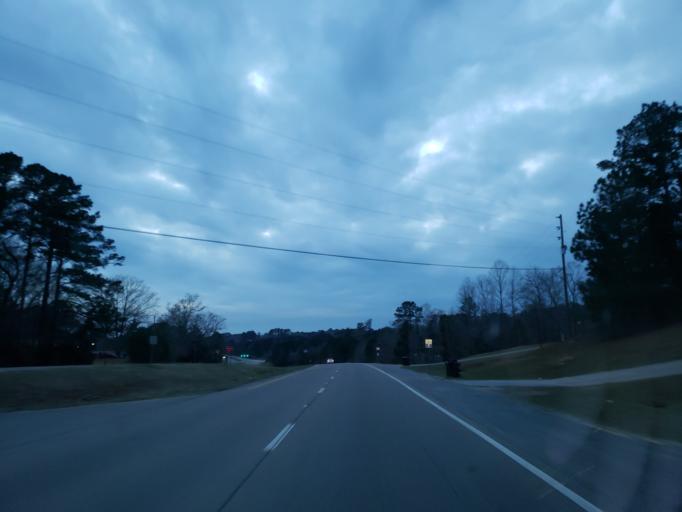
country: US
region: Mississippi
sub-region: Lauderdale County
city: Marion
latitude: 32.3672
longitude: -88.6459
